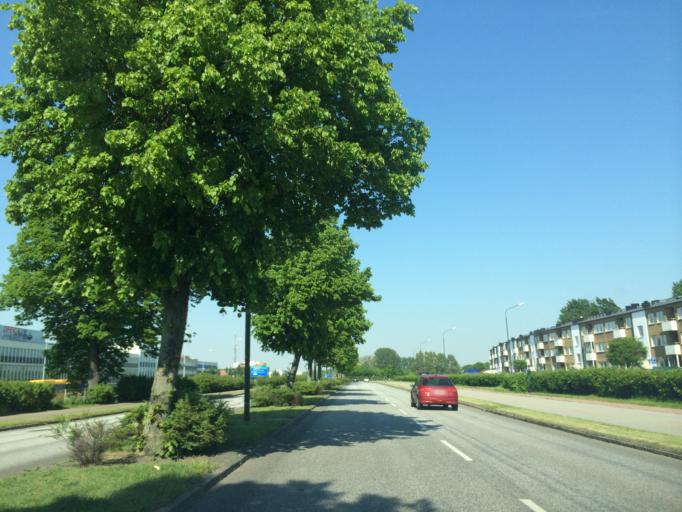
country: SE
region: Skane
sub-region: Burlovs Kommun
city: Arloev
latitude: 55.6165
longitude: 13.0470
